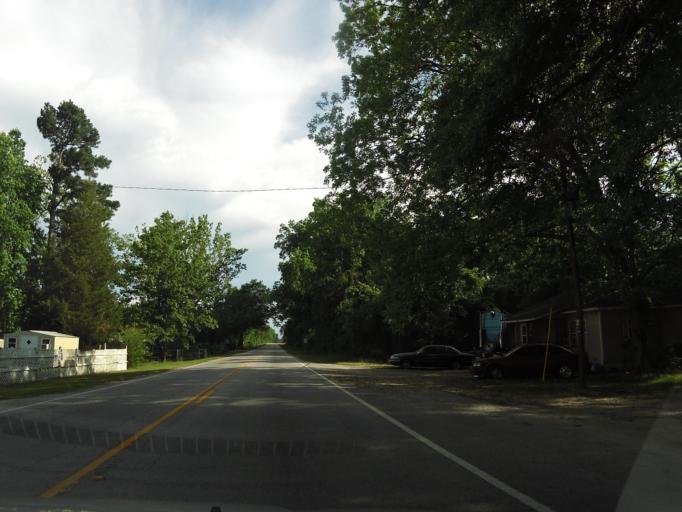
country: US
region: South Carolina
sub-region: Allendale County
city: Fairfax
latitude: 32.8585
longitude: -81.2381
